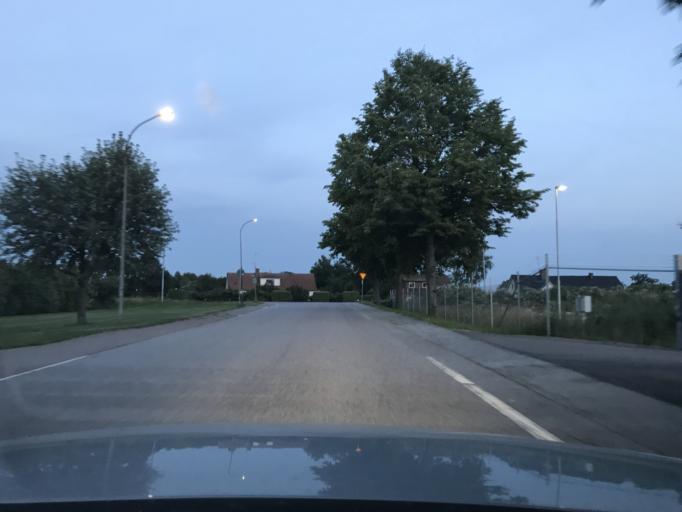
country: SE
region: Skane
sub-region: Svalovs Kommun
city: Svaloev
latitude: 55.9087
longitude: 13.0927
